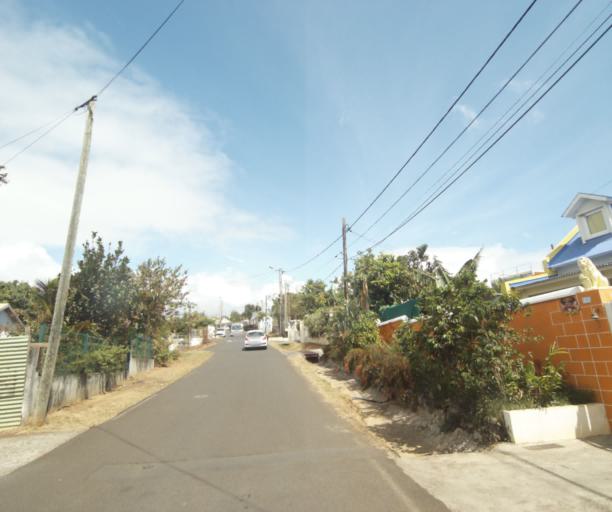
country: RE
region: Reunion
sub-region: Reunion
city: Saint-Paul
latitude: -21.0563
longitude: 55.2611
